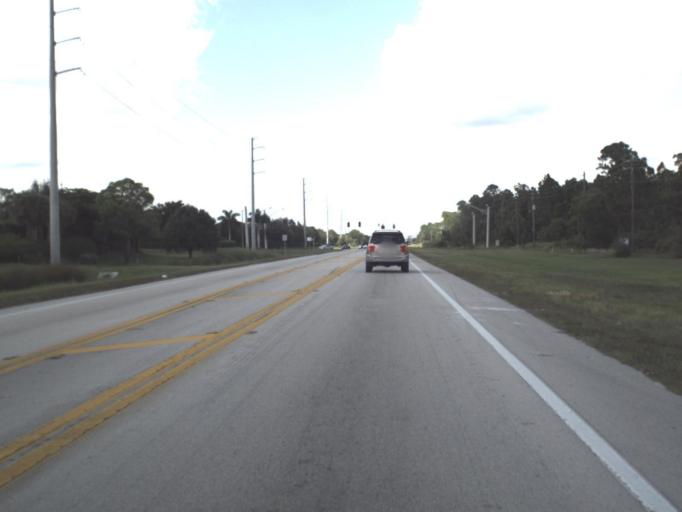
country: US
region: Florida
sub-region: Lee County
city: Gateway
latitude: 26.6066
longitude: -81.7540
